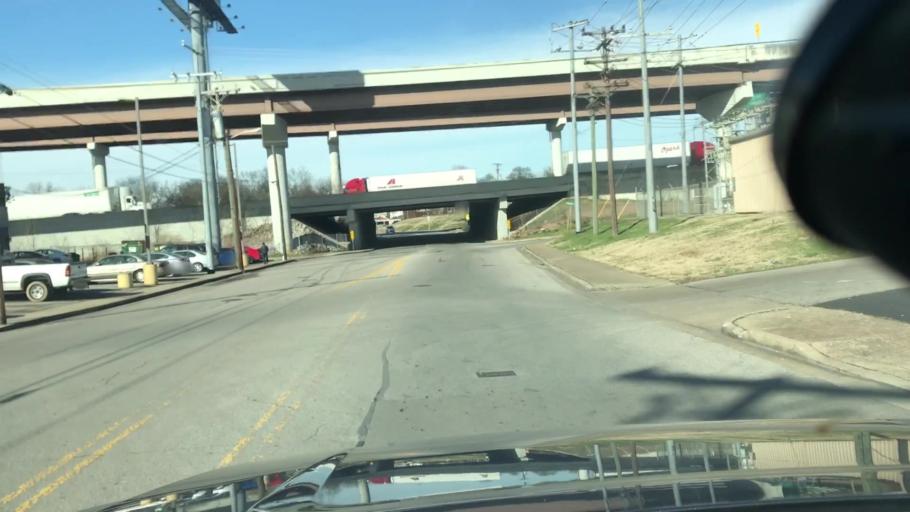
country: US
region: Tennessee
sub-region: Davidson County
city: Belle Meade
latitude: 36.1523
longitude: -86.8522
